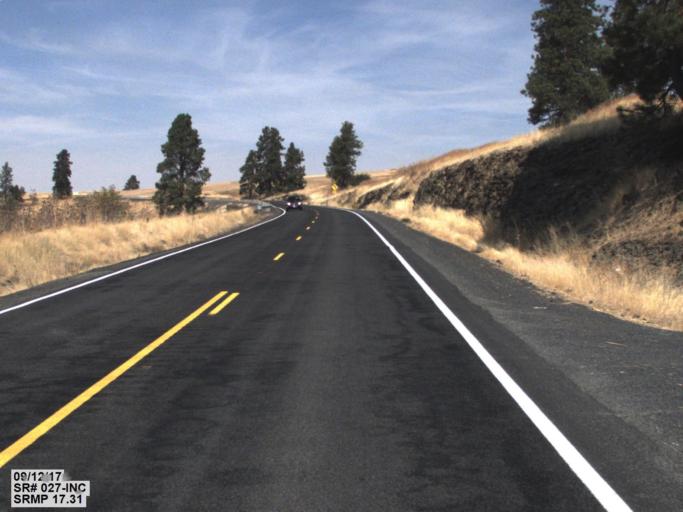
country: US
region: Washington
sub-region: Whitman County
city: Pullman
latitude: 46.9347
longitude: -117.0963
